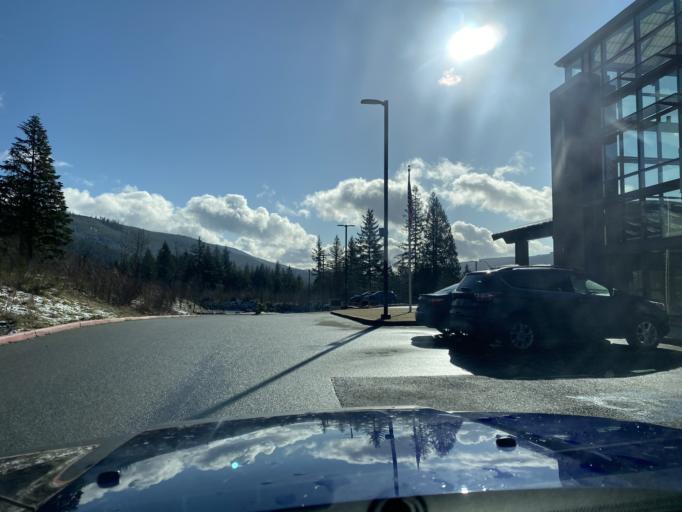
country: US
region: Washington
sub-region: King County
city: Fall City
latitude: 47.5130
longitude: -121.8852
